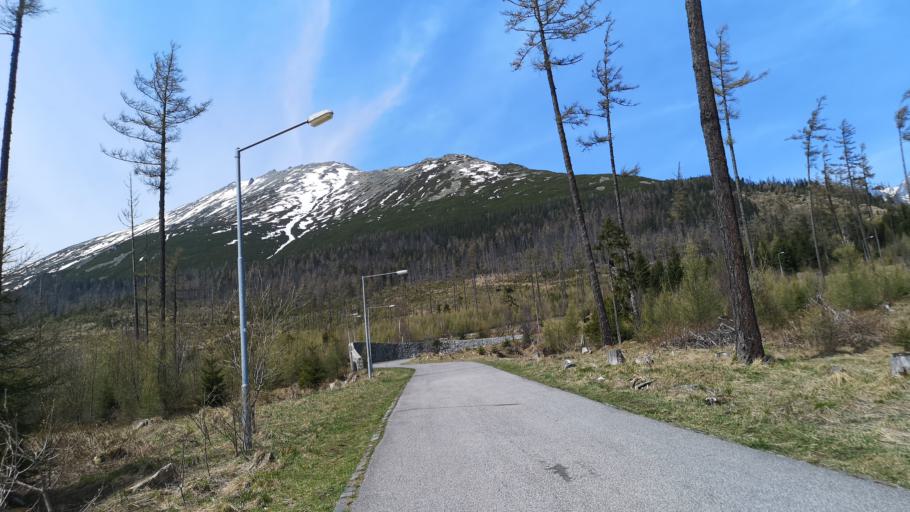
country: SK
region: Presovsky
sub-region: Okres Poprad
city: Vysoke Tatry
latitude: 49.1542
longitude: 20.2252
